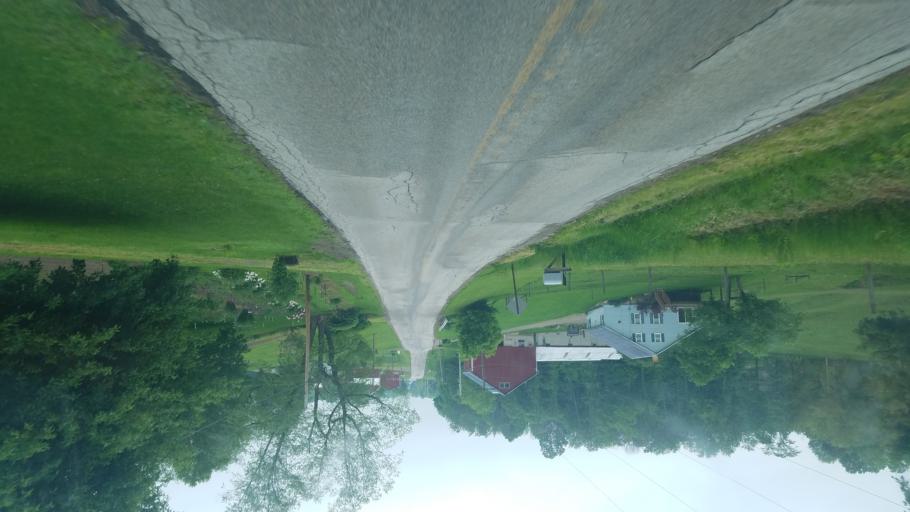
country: US
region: Ohio
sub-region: Sandusky County
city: Bellville
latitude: 40.6654
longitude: -82.4726
